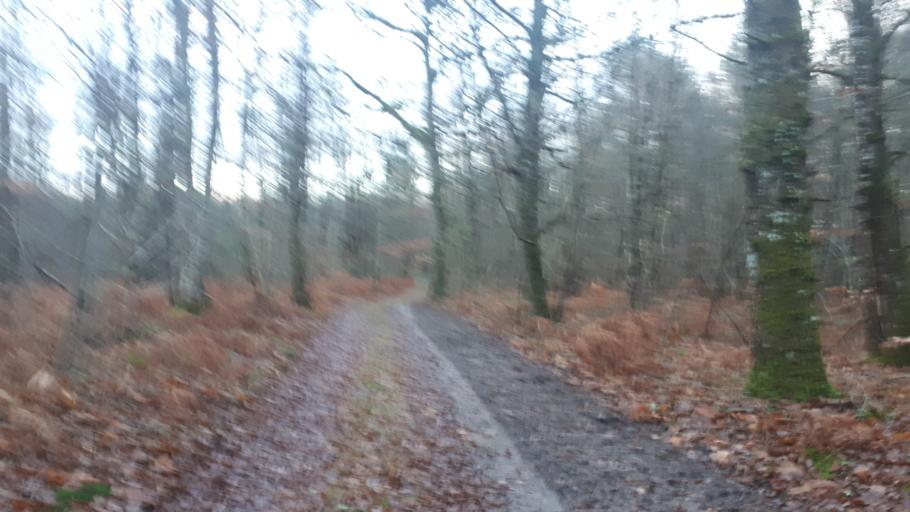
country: FR
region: Centre
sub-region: Departement du Loir-et-Cher
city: Saint-Romain-sur-Cher
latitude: 47.3421
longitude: 1.3958
